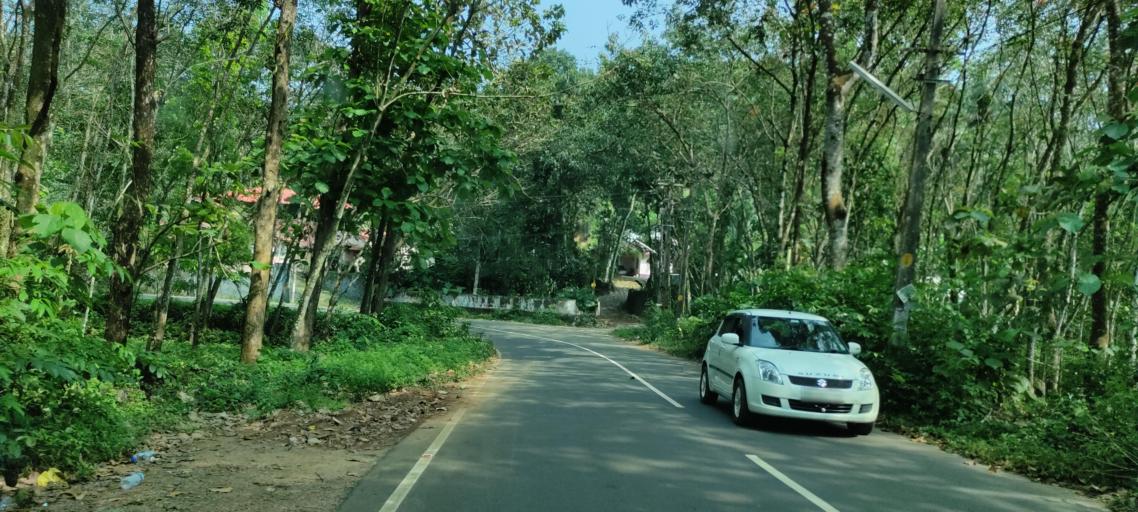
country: IN
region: Kerala
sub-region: Pattanamtitta
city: Adur
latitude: 9.2358
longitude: 76.6914
